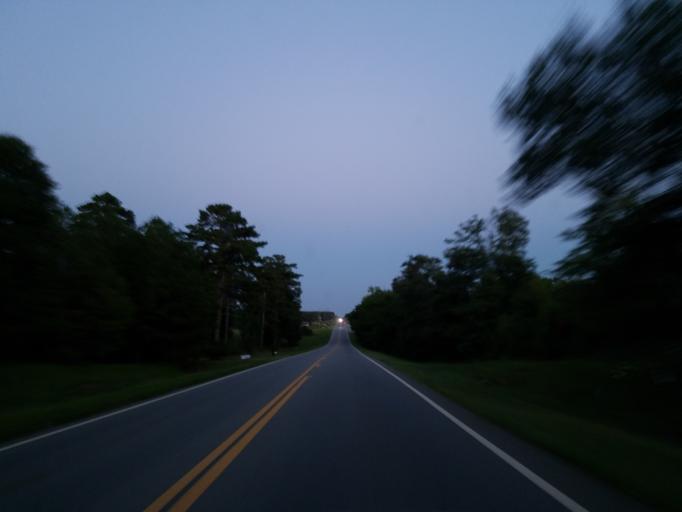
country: US
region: Georgia
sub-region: Dooly County
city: Unadilla
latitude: 32.3384
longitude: -83.7737
